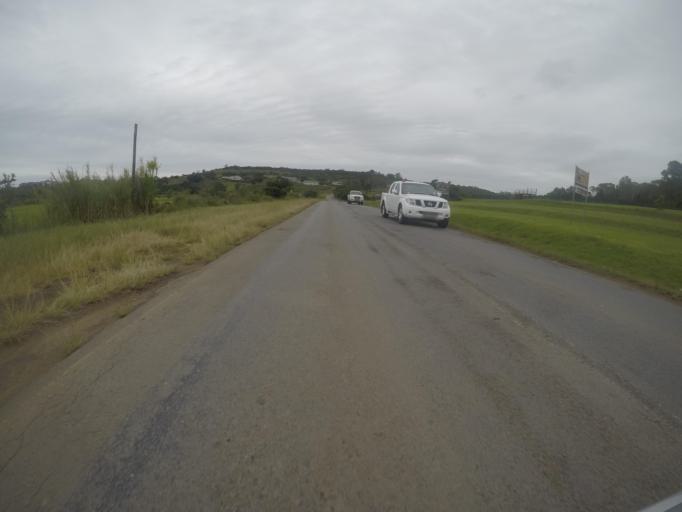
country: ZA
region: Eastern Cape
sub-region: Buffalo City Metropolitan Municipality
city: East London
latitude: -32.9402
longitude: 27.9388
